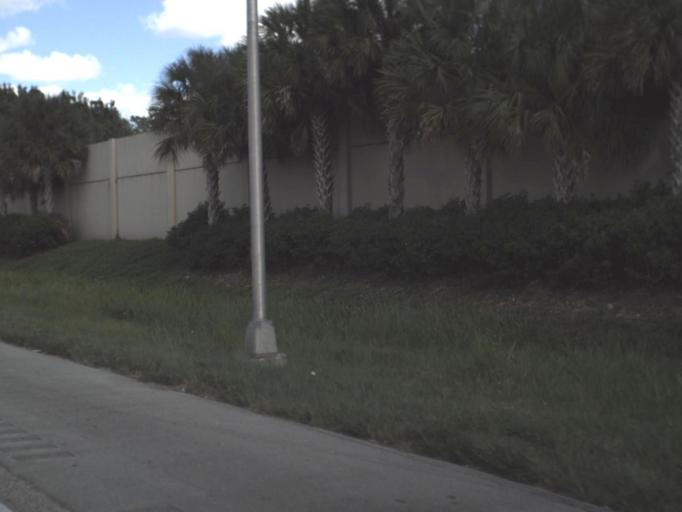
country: US
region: Florida
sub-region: Broward County
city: Coral Springs
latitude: 26.2576
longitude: -80.2969
